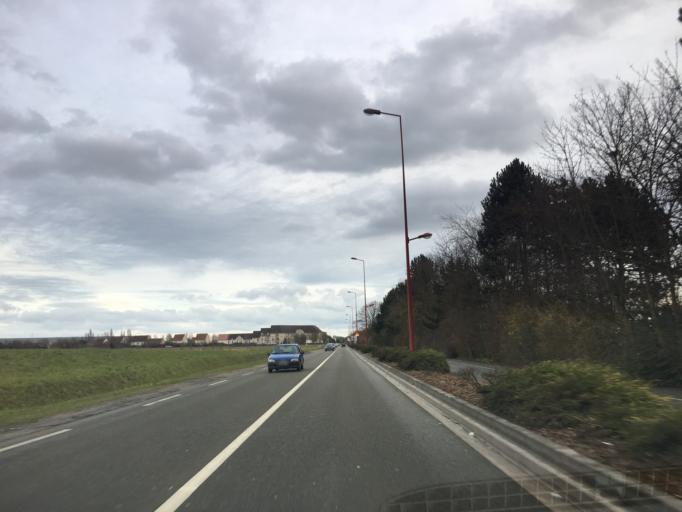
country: FR
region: Ile-de-France
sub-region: Departement du Val-d'Oise
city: Gonesse
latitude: 48.9955
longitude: 2.4390
